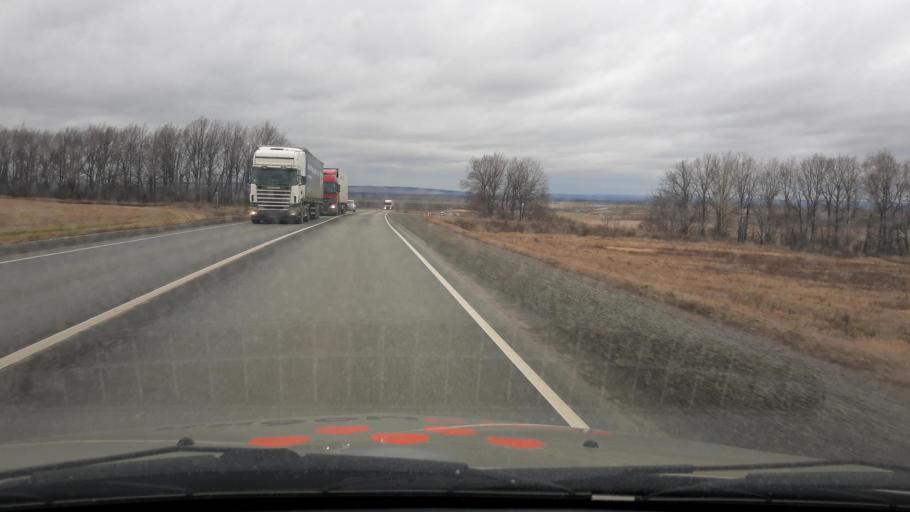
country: RU
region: Bashkortostan
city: Avdon
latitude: 54.8535
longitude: 55.7038
